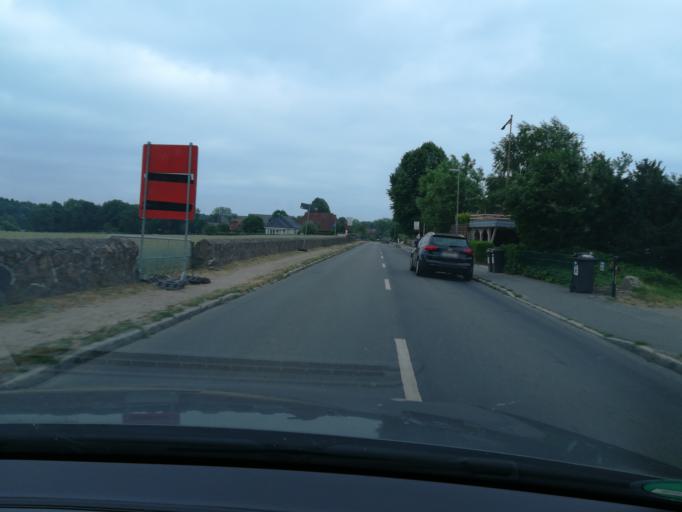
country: DE
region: Schleswig-Holstein
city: Grossensee
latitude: 53.6197
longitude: 10.3389
